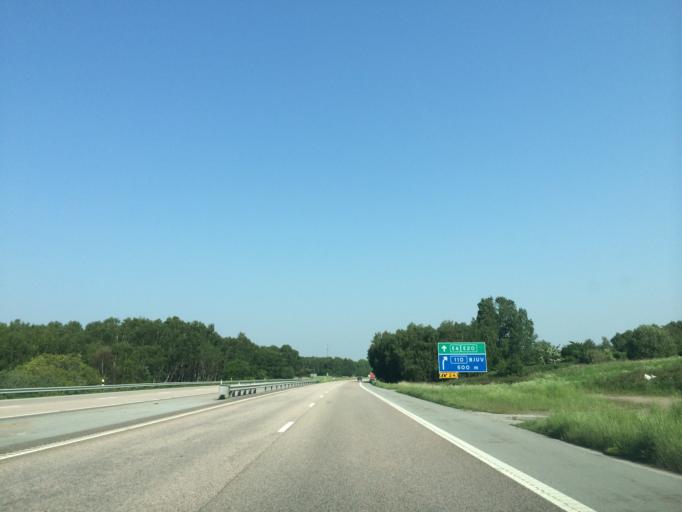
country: SE
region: Skane
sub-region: Kavlinge Kommun
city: Hofterup
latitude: 55.8140
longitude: 12.9431
